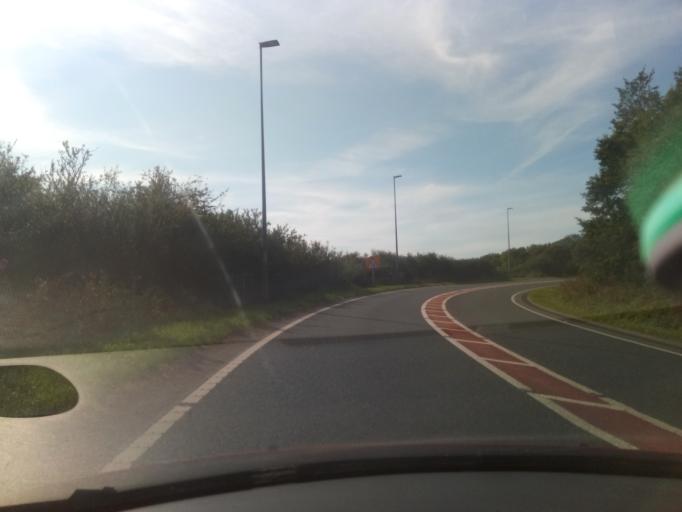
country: GB
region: England
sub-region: Stockton-on-Tees
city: Yarm
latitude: 54.4708
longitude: -1.3231
